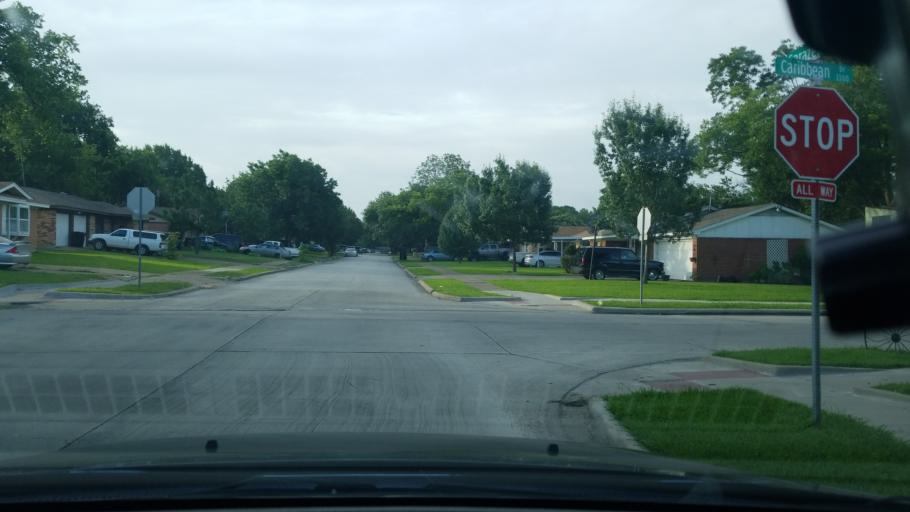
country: US
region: Texas
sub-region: Dallas County
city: Mesquite
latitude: 32.8309
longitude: -96.6496
